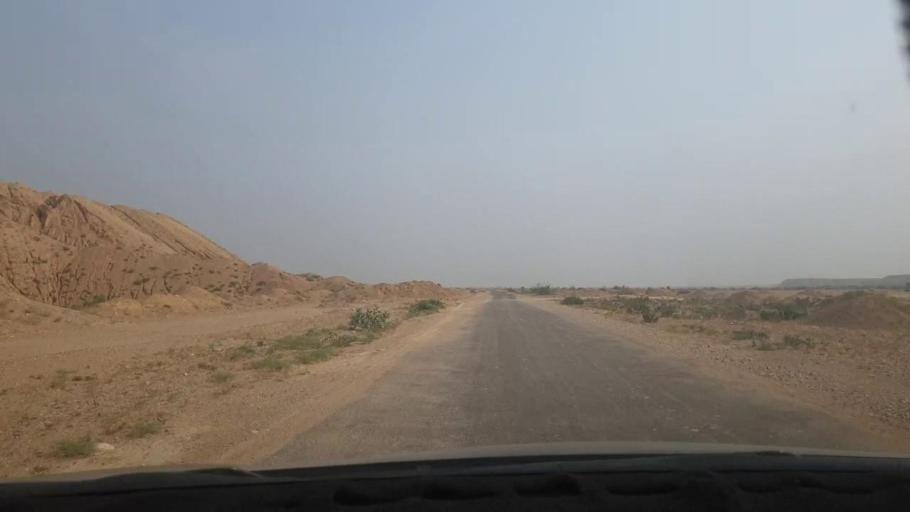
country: PK
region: Sindh
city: Matiari
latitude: 25.5798
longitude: 68.3147
